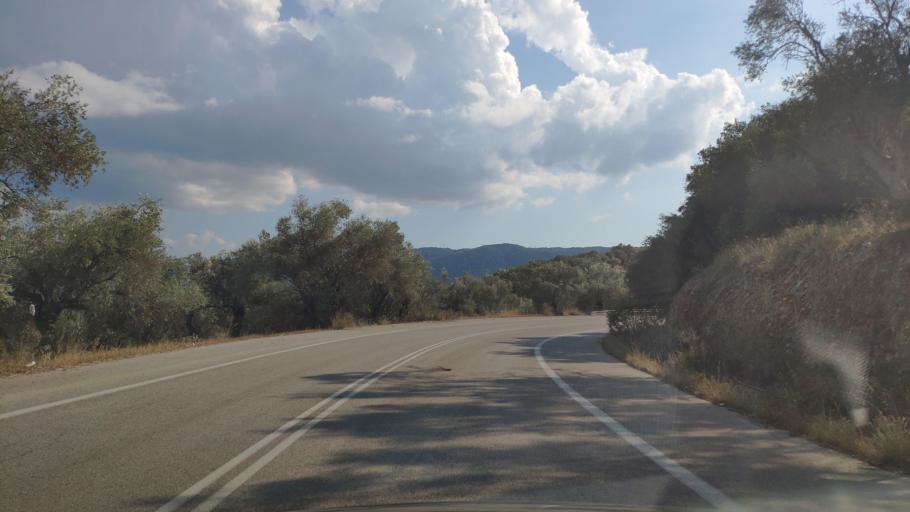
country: GR
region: West Greece
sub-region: Nomos Aitolias kai Akarnanias
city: Stanos
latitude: 38.7731
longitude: 21.1829
